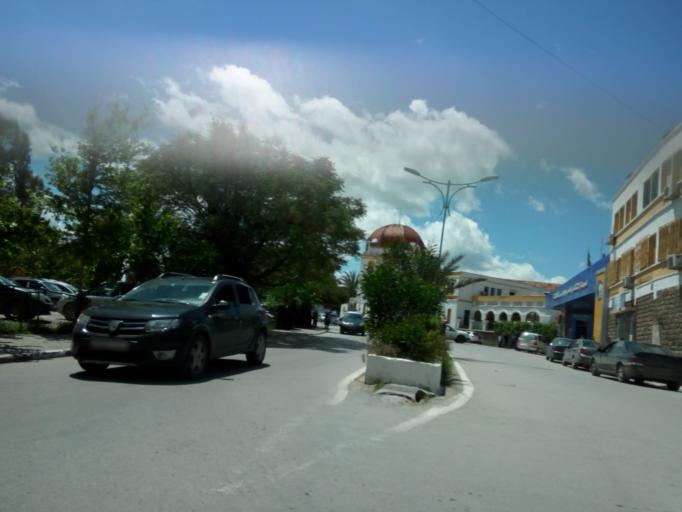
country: DZ
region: Constantine
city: Constantine
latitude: 36.3738
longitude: 6.6189
